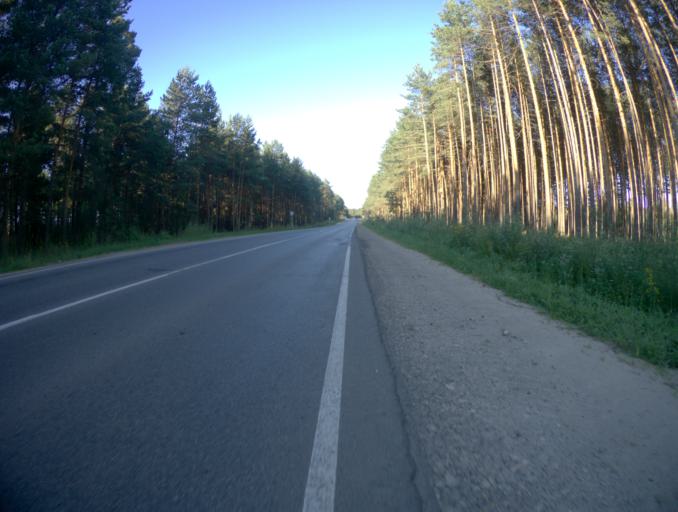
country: RU
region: Vladimir
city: Golovino
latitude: 56.0351
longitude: 40.4185
